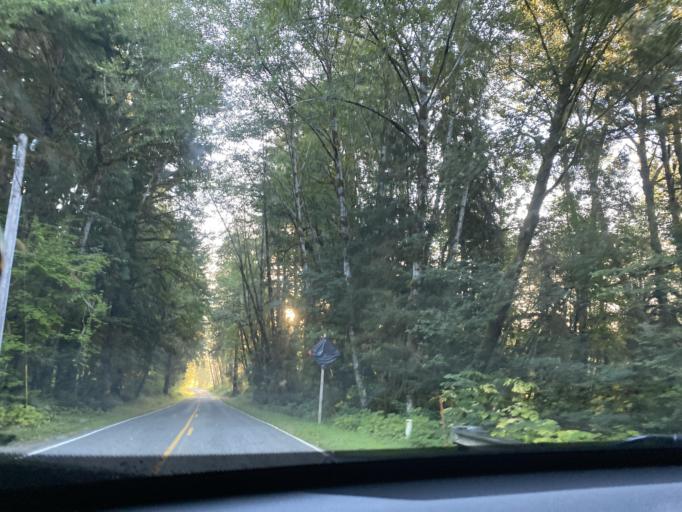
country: US
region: Washington
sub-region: Clallam County
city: Forks
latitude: 47.8225
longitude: -124.1986
